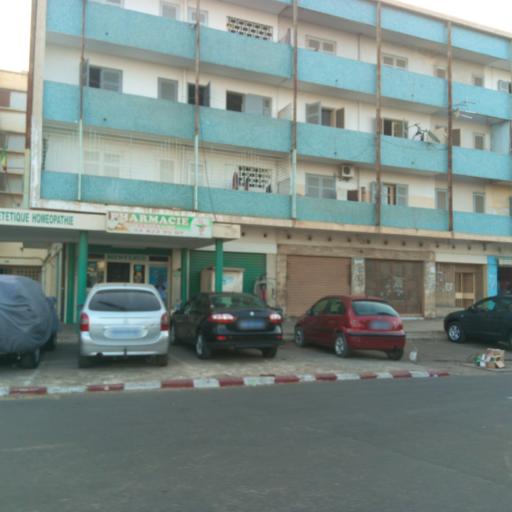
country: SN
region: Dakar
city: Dakar
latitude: 14.6869
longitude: -17.4457
